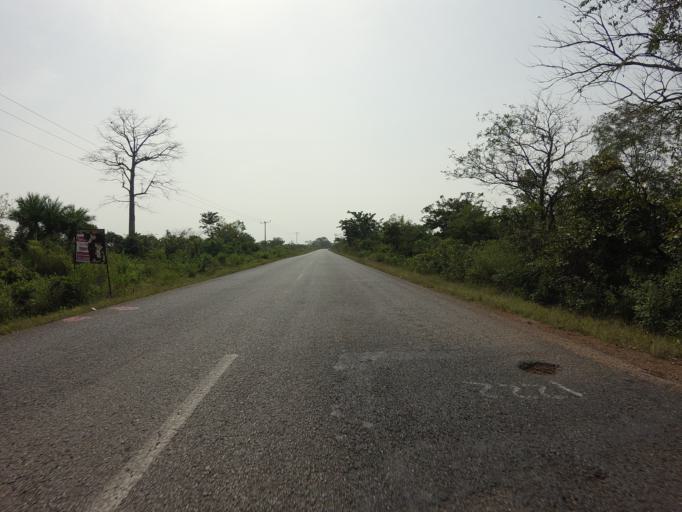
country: GH
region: Volta
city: Ho
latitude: 6.3922
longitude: 0.1820
